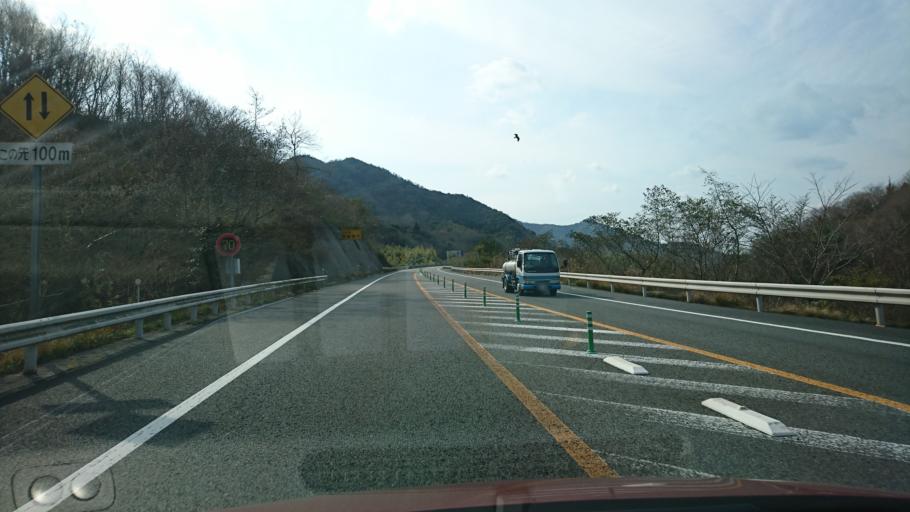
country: JP
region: Hiroshima
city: Innoshima
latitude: 34.1369
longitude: 133.0531
